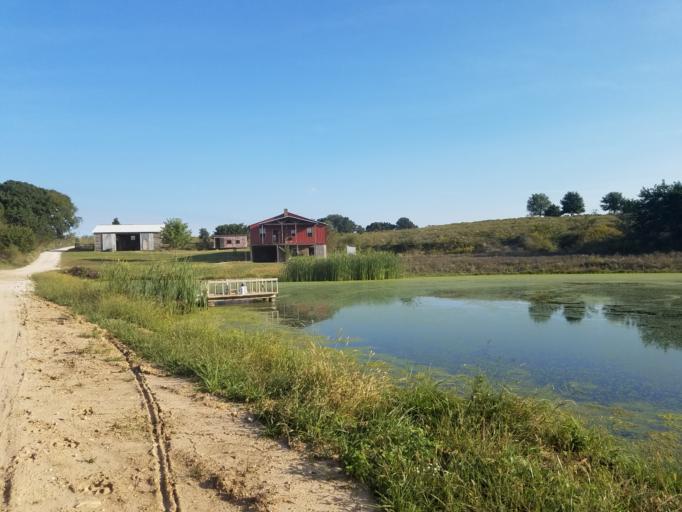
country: US
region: Missouri
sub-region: Cooper County
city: Boonville
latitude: 38.8524
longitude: -92.6456
